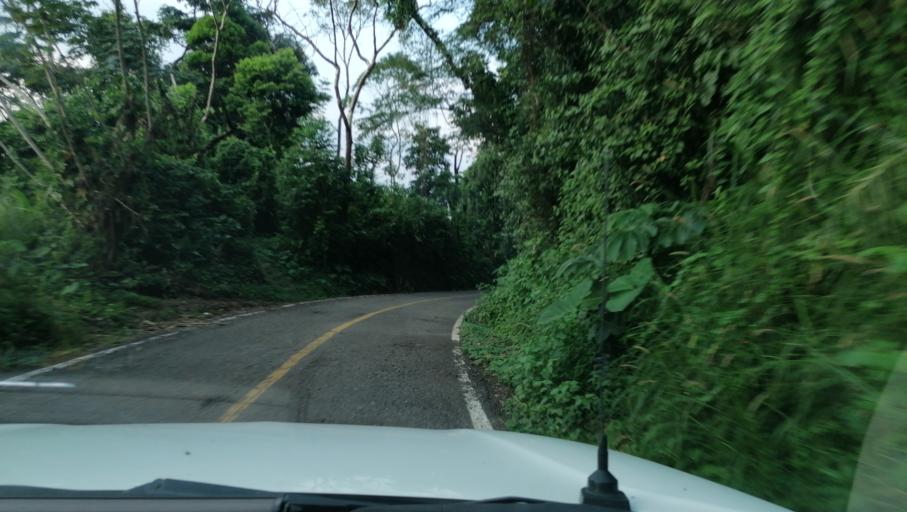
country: MX
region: Chiapas
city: Pichucalco
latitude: 17.5084
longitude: -93.2121
